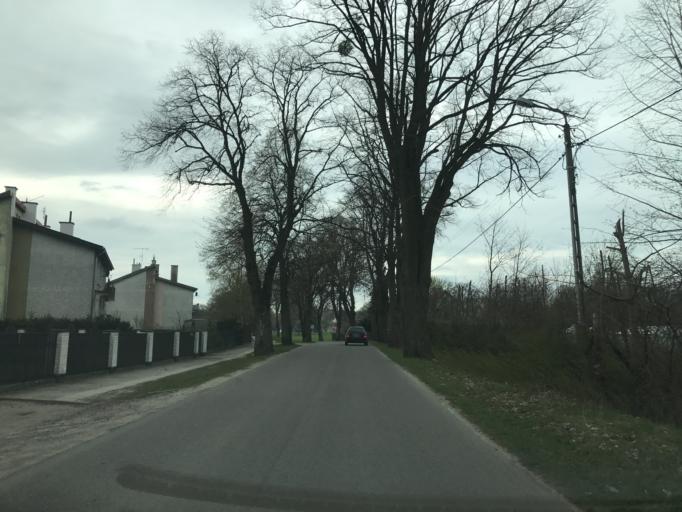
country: PL
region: Warmian-Masurian Voivodeship
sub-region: Powiat olsztynski
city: Olsztynek
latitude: 53.5876
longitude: 20.2812
